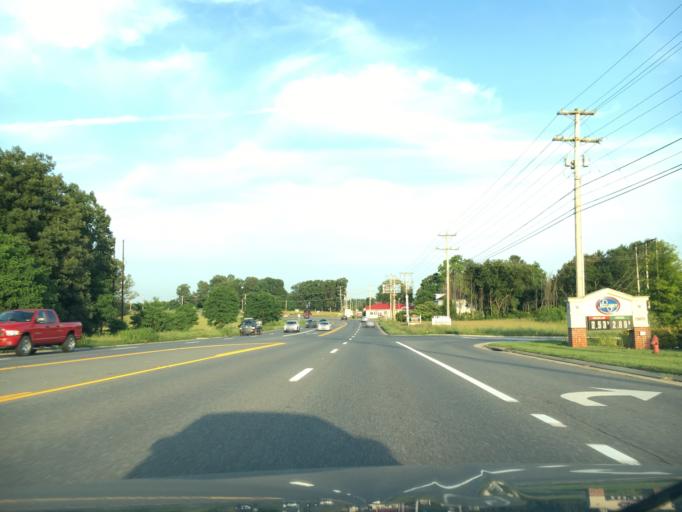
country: US
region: Virginia
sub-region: Bedford County
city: Forest
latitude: 37.3653
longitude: -79.2937
